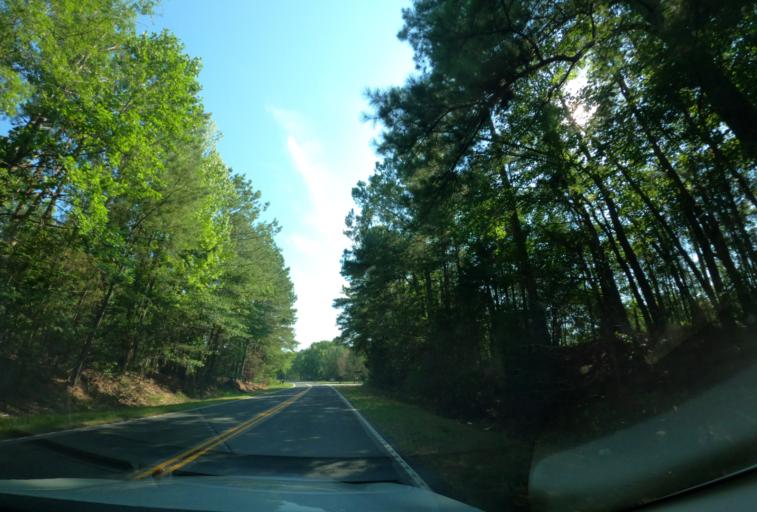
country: US
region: South Carolina
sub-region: Anderson County
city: Belton
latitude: 34.4363
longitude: -82.5531
